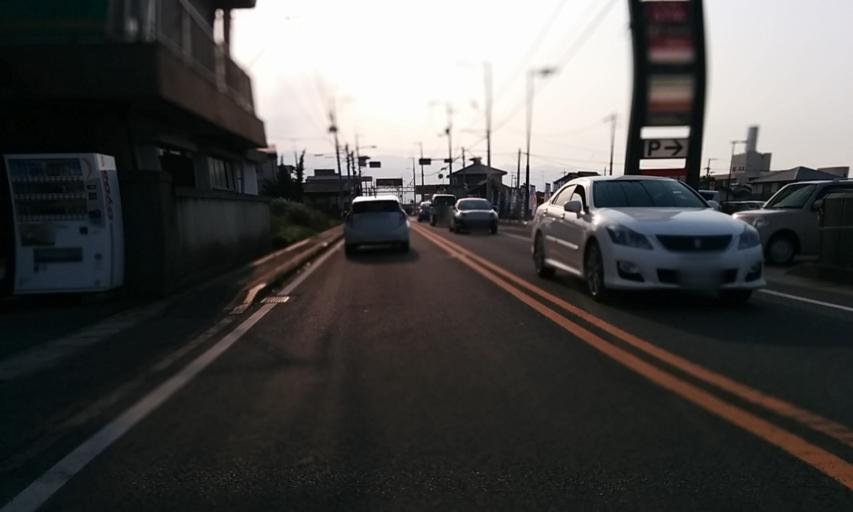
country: JP
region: Ehime
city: Saijo
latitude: 33.8960
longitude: 133.1254
